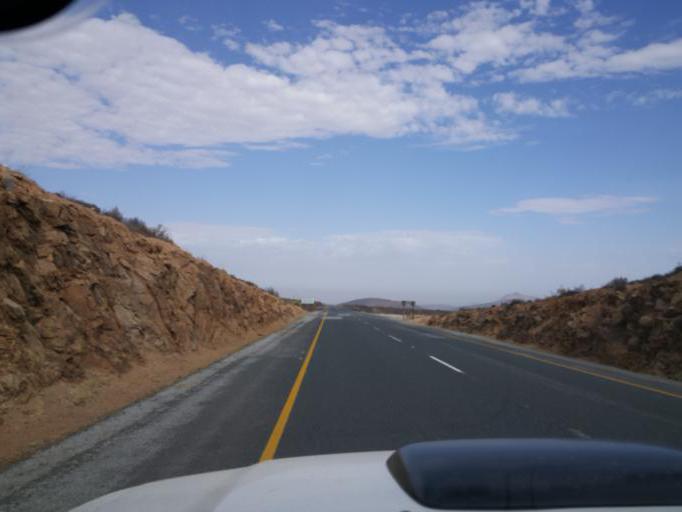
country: ZA
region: Northern Cape
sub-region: Namakwa District Municipality
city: Springbok
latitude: -29.2212
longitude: 17.6529
